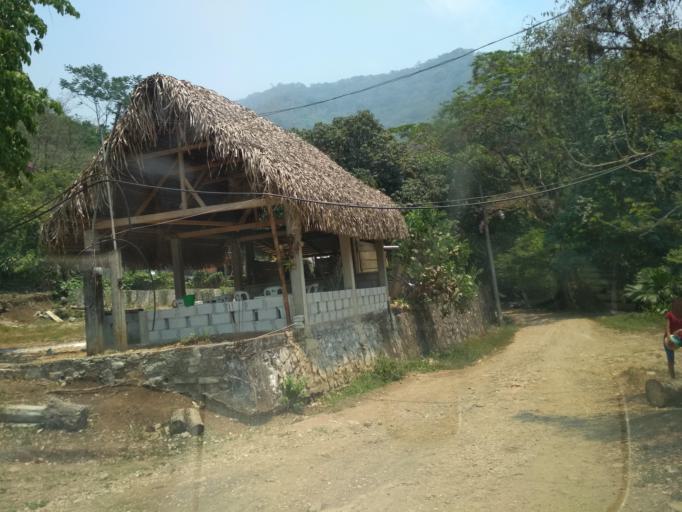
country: MX
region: Veracruz
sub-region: Tezonapa
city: Laguna Chica (Pueblo Nuevo)
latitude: 18.5679
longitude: -96.7304
